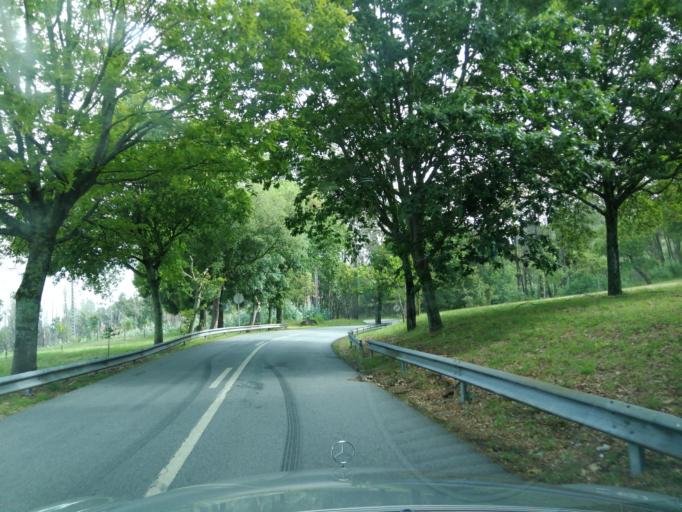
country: PT
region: Braga
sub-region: Braga
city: Braga
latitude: 41.5439
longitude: -8.3731
